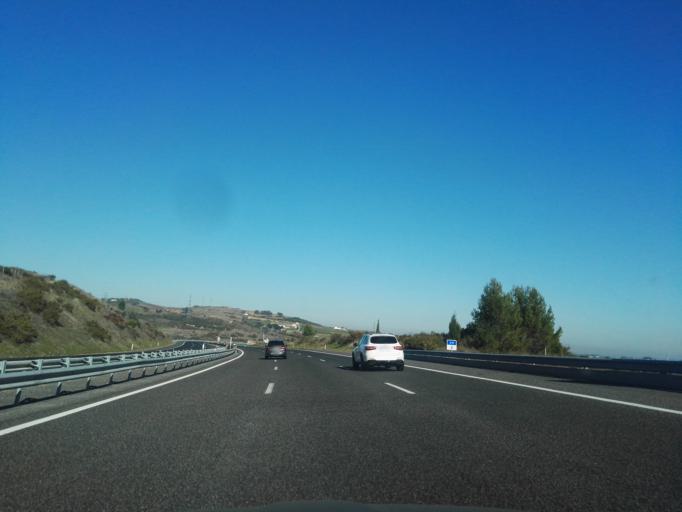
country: PT
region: Lisbon
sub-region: Vila Franca de Xira
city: Sobralinho
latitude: 38.9289
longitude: -9.0739
